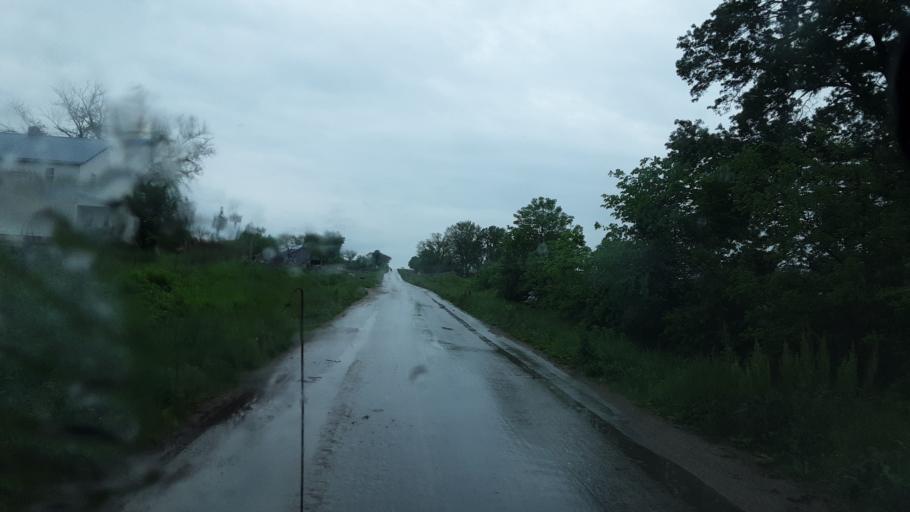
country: US
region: Missouri
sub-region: Randolph County
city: Moberly
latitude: 39.3558
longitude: -92.2684
